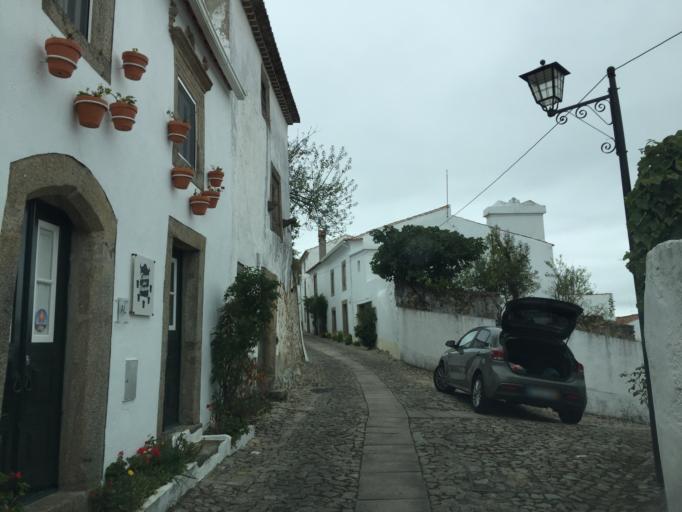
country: PT
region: Portalegre
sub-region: Marvao
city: Marvao
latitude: 39.3929
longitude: -7.3759
